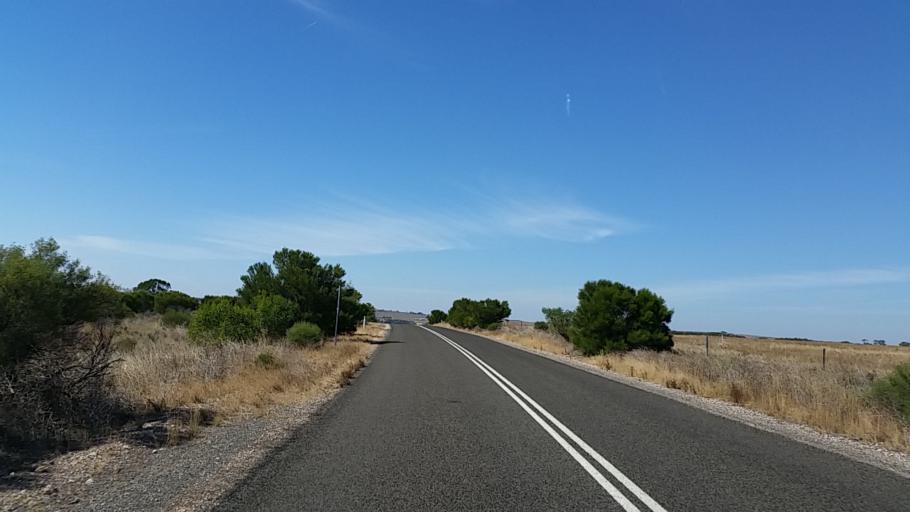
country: AU
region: South Australia
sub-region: Mid Murray
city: Mannum
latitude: -34.7502
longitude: 139.5492
